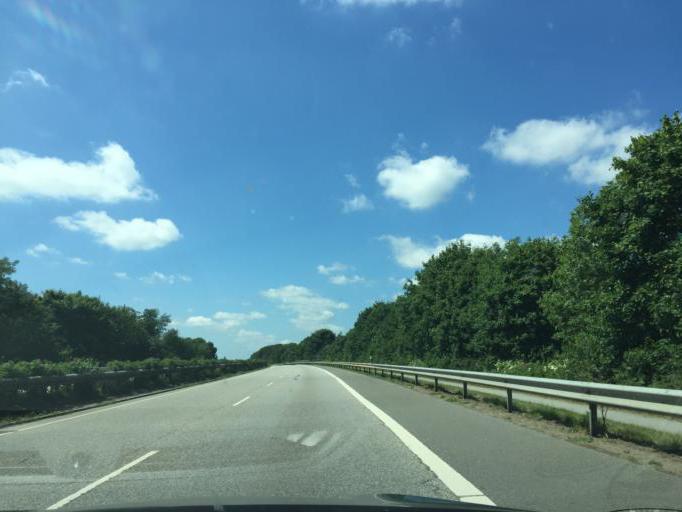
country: DE
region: Schleswig-Holstein
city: Harrislee
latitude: 54.7772
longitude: 9.3877
